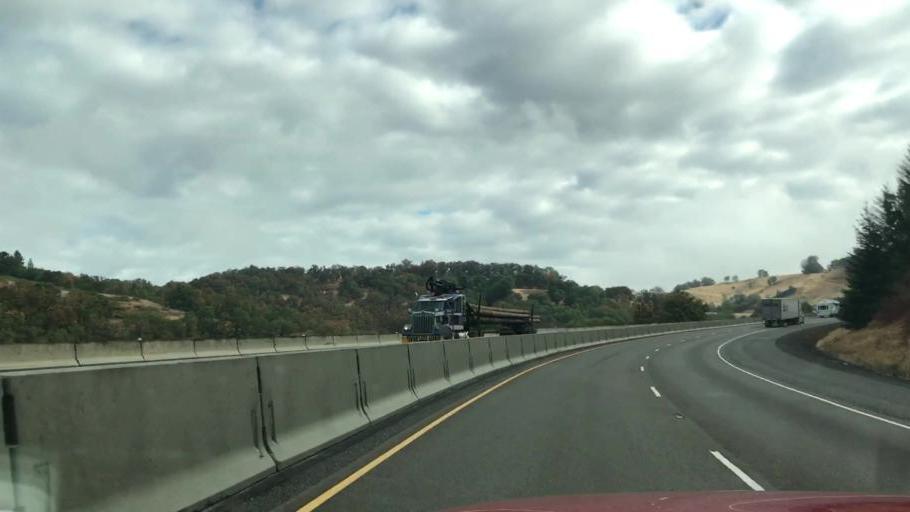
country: US
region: Oregon
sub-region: Douglas County
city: Winston
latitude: 43.1045
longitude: -123.3649
